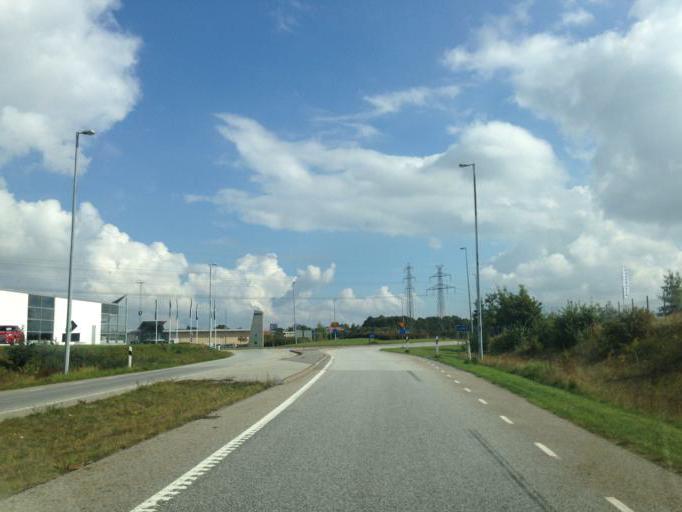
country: SE
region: Skane
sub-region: Lunds Kommun
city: Lund
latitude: 55.7126
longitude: 13.1551
